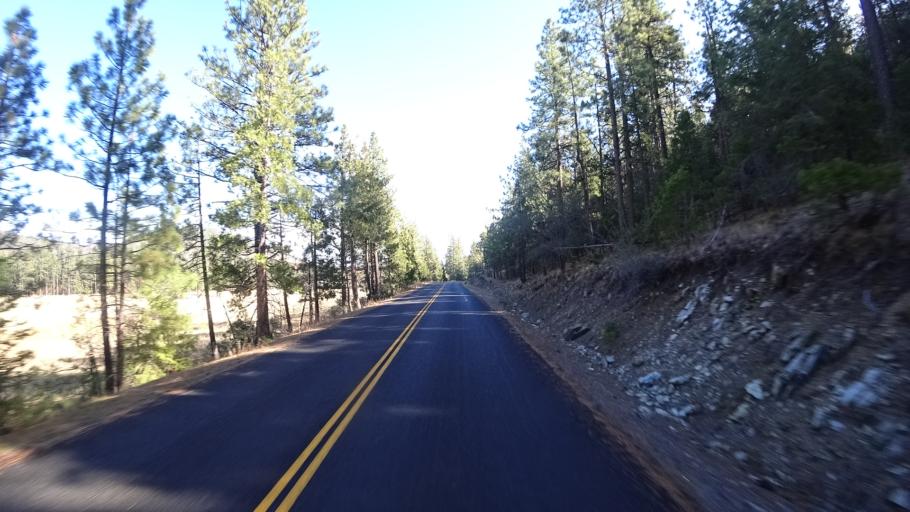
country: US
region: California
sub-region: Siskiyou County
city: Weed
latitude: 41.4324
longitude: -122.4881
